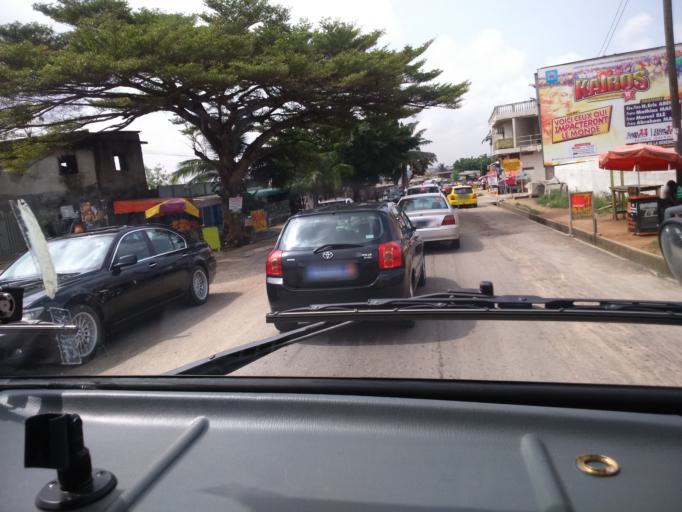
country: CI
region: Lagunes
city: Abobo
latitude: 5.3694
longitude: -3.9806
